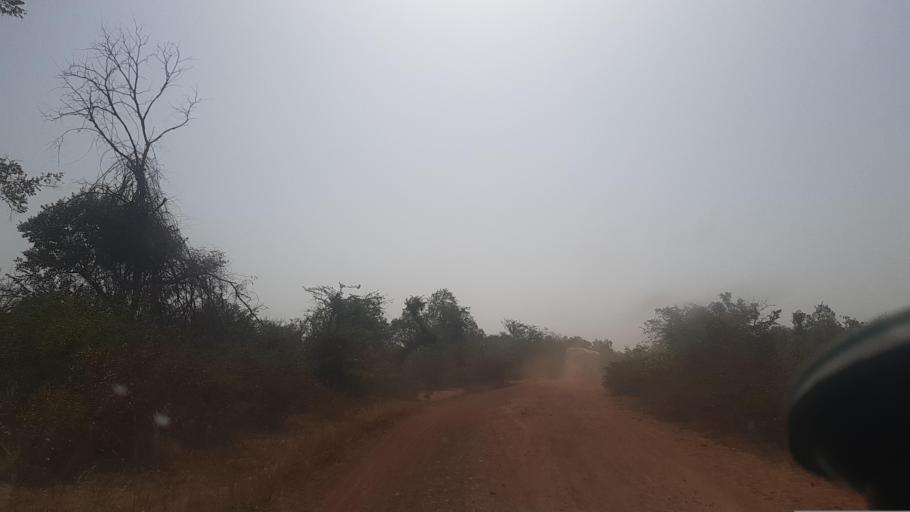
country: ML
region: Segou
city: Baroueli
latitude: 13.0738
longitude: -6.4811
